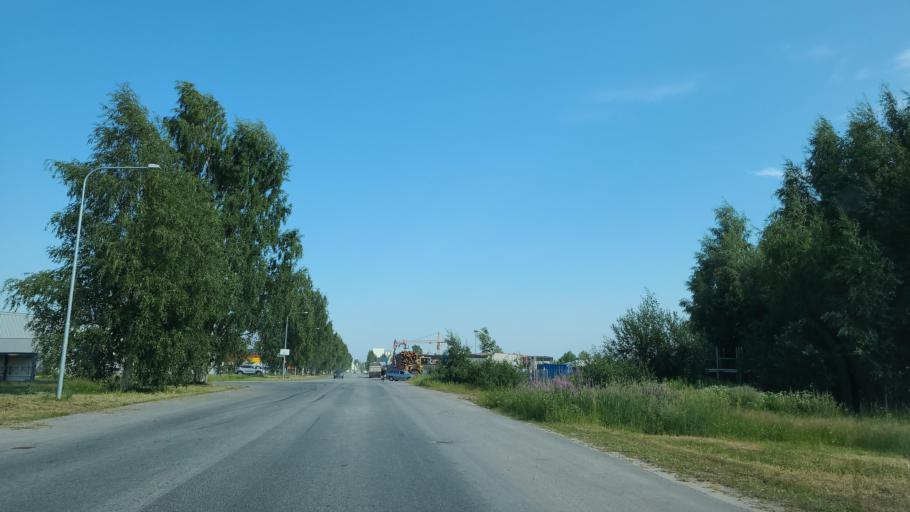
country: SE
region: Vaesterbotten
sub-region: Umea Kommun
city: Umea
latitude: 63.8456
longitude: 20.2170
